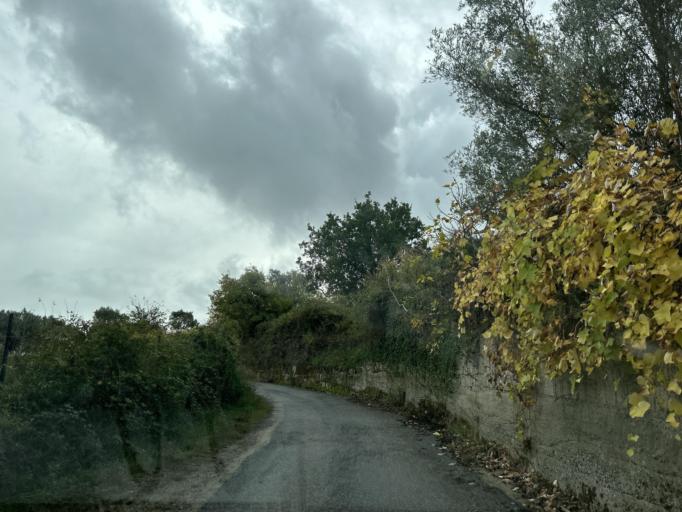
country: IT
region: Calabria
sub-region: Provincia di Catanzaro
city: Staletti
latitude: 38.7699
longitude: 16.5305
